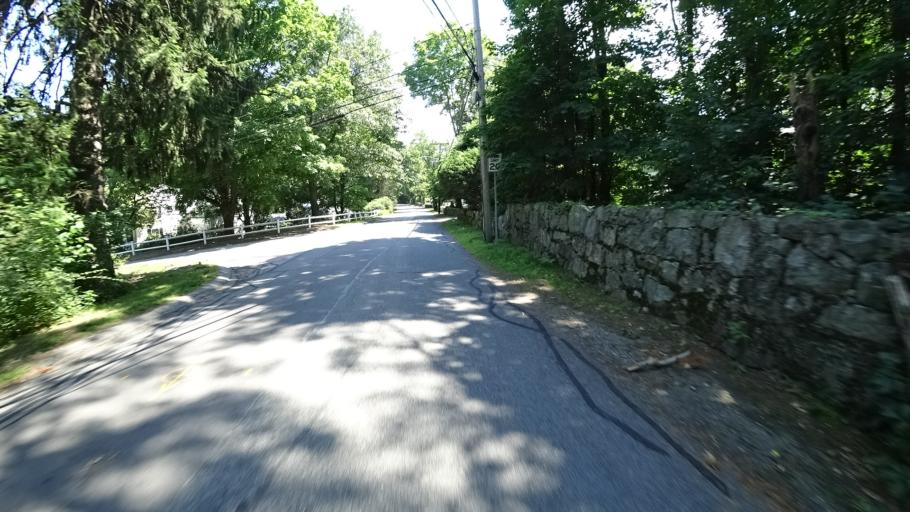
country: US
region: Massachusetts
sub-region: Norfolk County
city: Dedham
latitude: 42.2530
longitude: -71.1914
